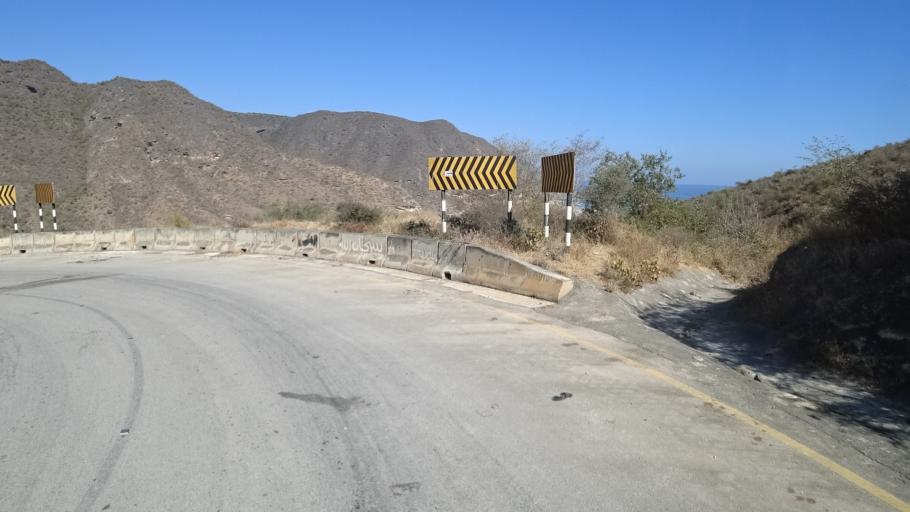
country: YE
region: Al Mahrah
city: Hawf
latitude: 16.7476
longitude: 53.4101
